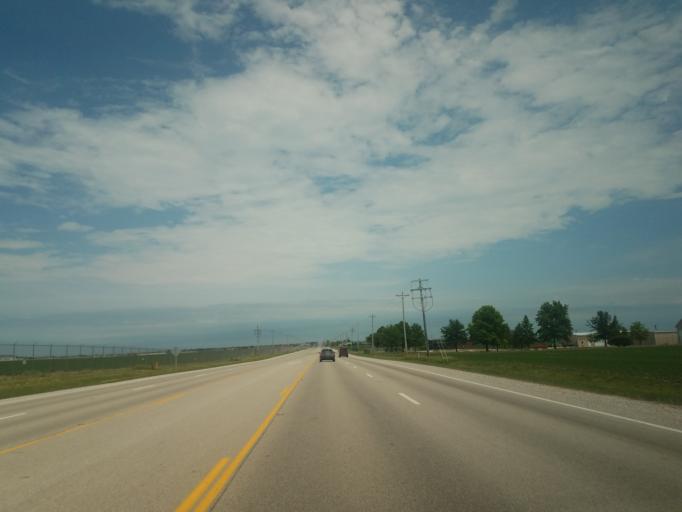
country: US
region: Illinois
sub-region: McLean County
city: Downs
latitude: 40.4766
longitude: -88.9023
